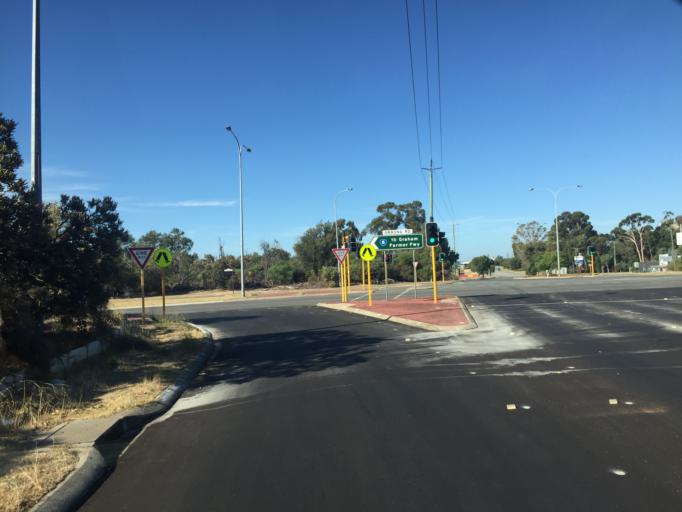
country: AU
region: Western Australia
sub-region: Canning
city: East Cannington
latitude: -31.9984
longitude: 115.9630
